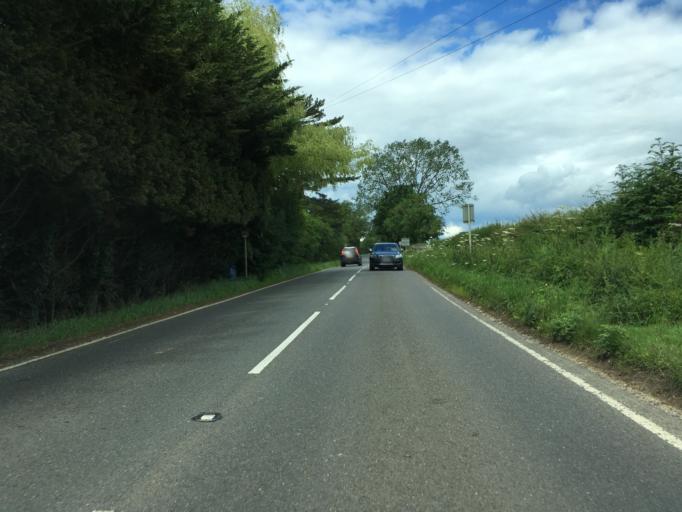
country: GB
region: England
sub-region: Northamptonshire
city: Brackley
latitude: 52.0703
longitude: -1.1051
